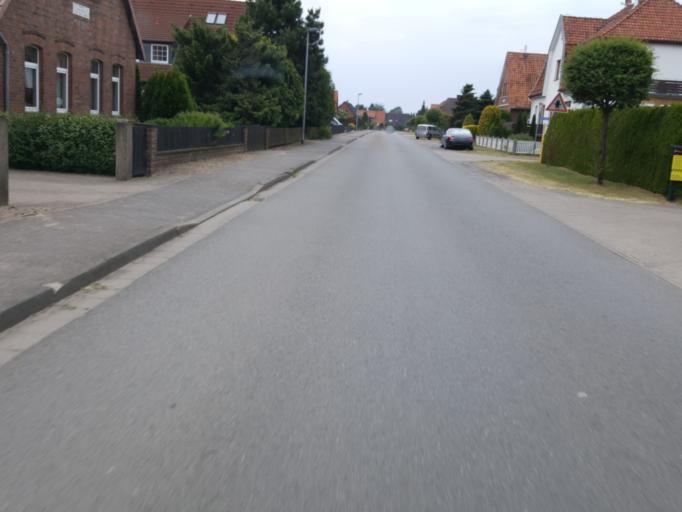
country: DE
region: Lower Saxony
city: Rehburg-Loccum
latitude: 52.4815
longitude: 9.2271
